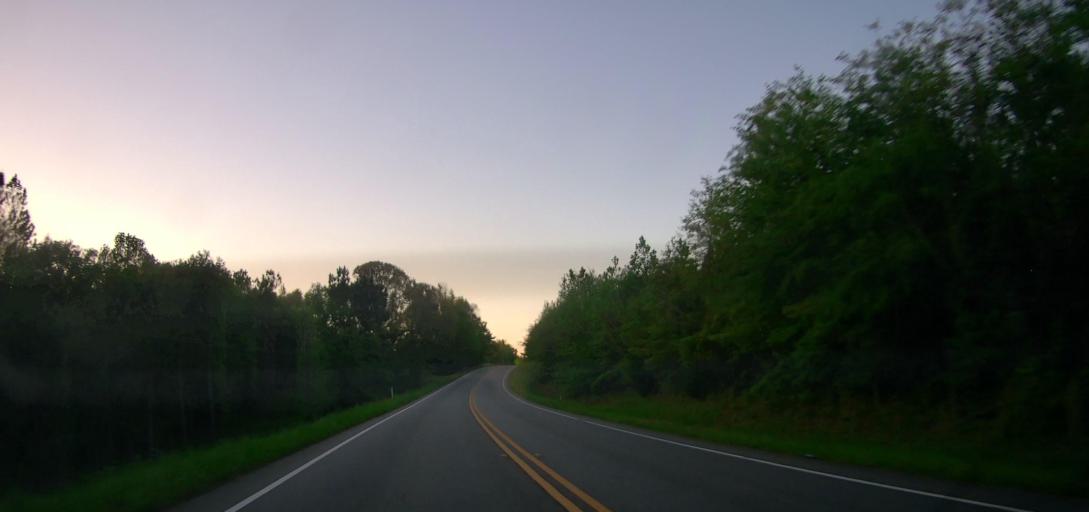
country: US
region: Georgia
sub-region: Marion County
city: Buena Vista
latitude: 32.3546
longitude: -84.5372
